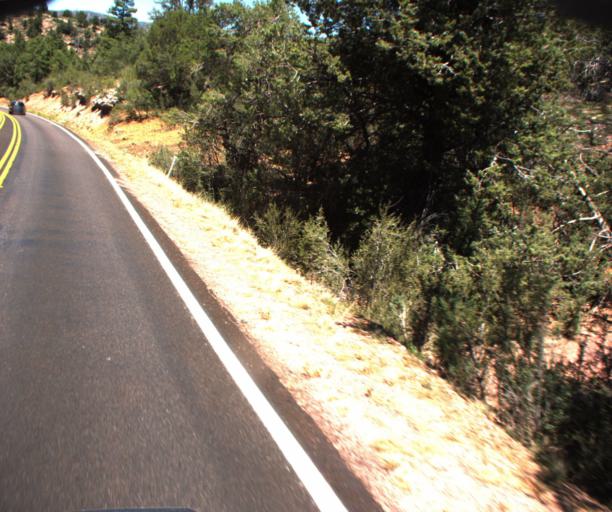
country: US
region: Arizona
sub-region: Gila County
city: Pine
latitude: 34.3616
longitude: -111.4256
